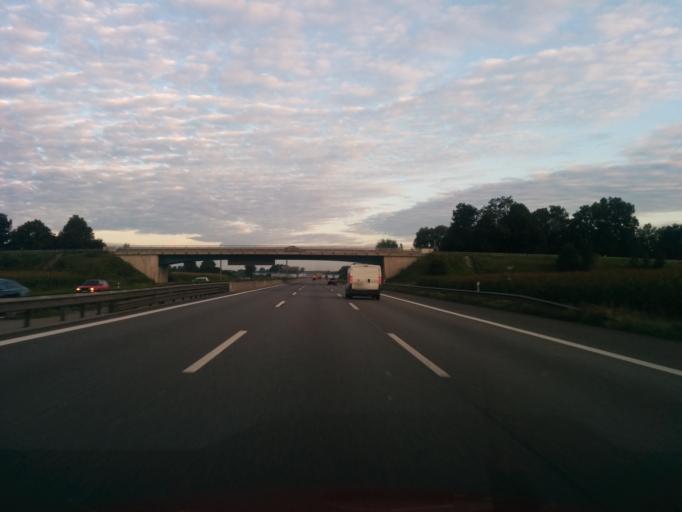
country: DE
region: Bavaria
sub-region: Upper Bavaria
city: Bergkirchen
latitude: 48.2393
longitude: 11.3378
